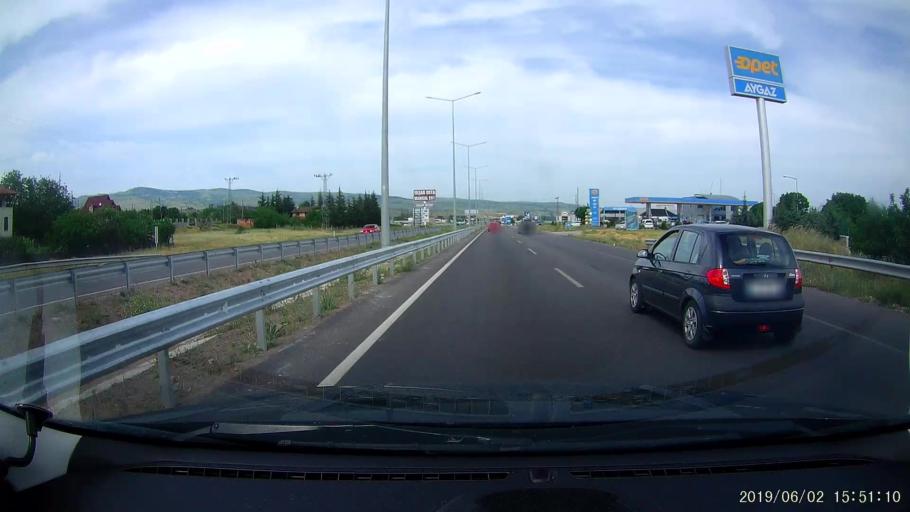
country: TR
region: Amasya
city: Merzifon
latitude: 40.8655
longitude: 35.4913
